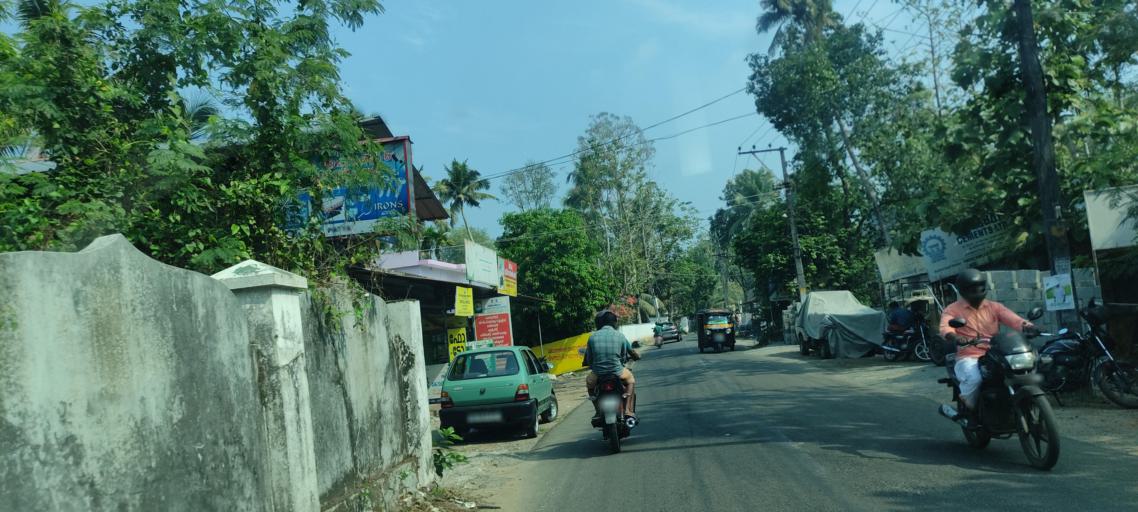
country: IN
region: Kerala
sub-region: Alappuzha
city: Kutiatodu
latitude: 9.7772
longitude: 76.3050
